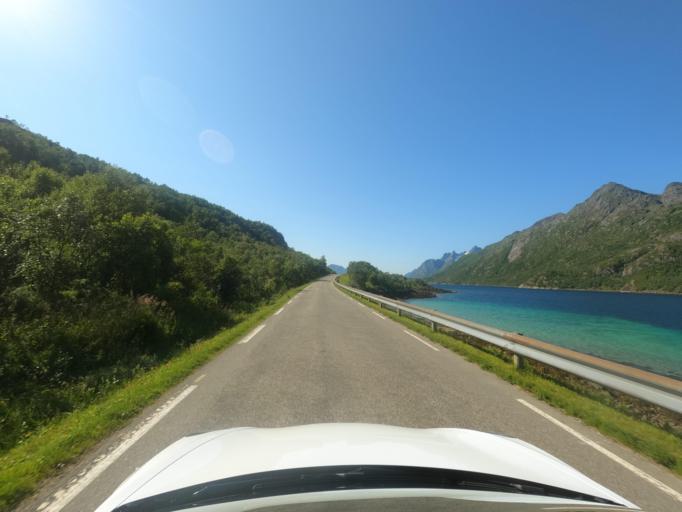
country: NO
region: Nordland
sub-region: Hadsel
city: Stokmarknes
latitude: 68.3879
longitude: 15.0964
